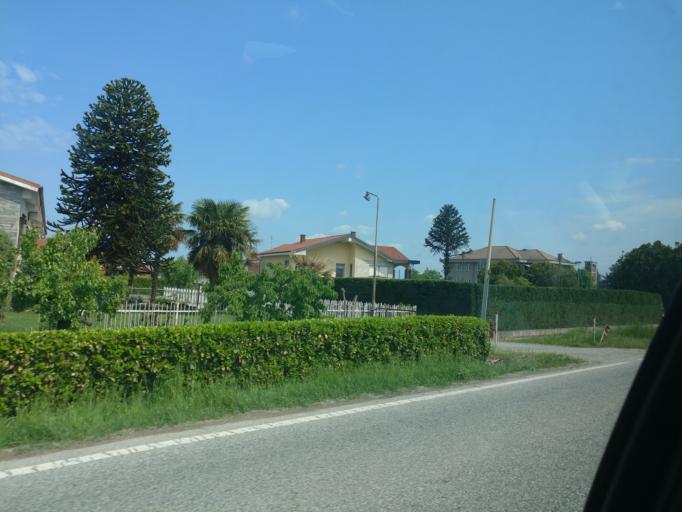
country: IT
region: Piedmont
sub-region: Provincia di Torino
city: Cavour
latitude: 44.7511
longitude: 7.4063
